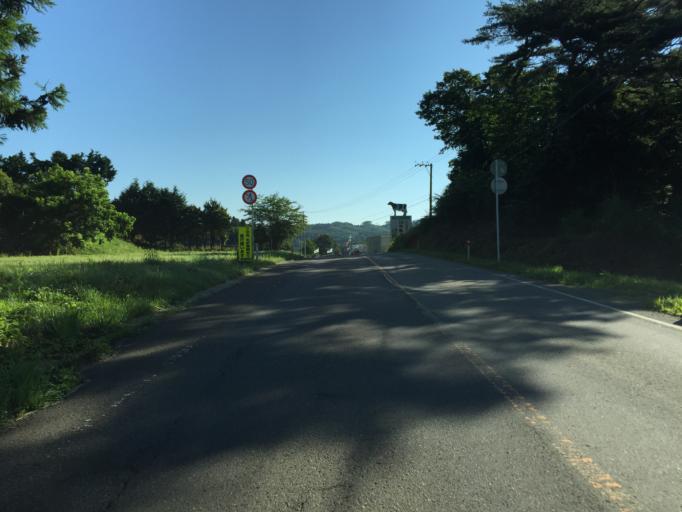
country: JP
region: Miyagi
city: Marumori
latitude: 37.7682
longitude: 140.7433
